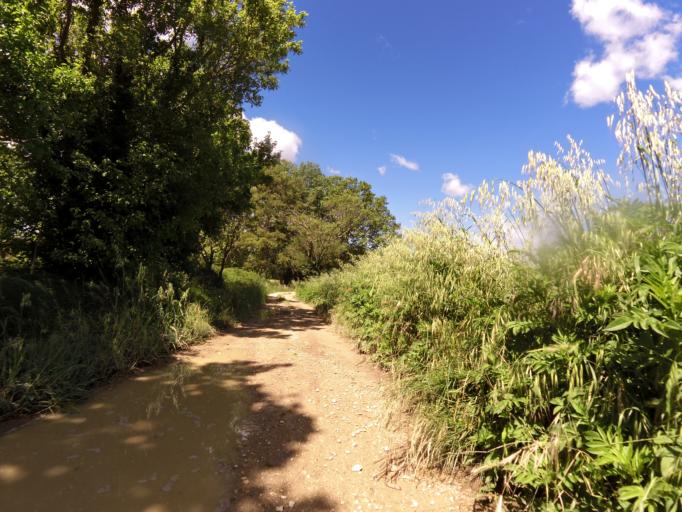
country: FR
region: Languedoc-Roussillon
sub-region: Departement du Gard
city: Vergeze
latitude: 43.7612
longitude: 4.2077
